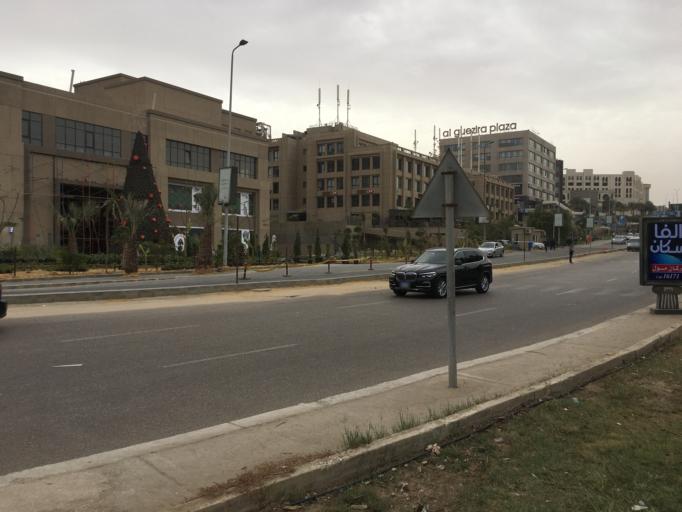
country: EG
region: Al Jizah
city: Awsim
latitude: 30.0218
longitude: 31.0040
